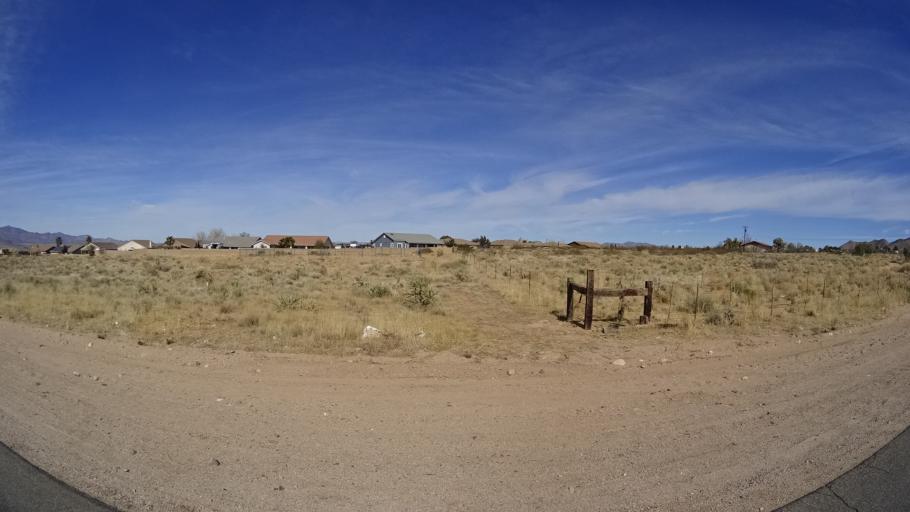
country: US
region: Arizona
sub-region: Mohave County
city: Kingman
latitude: 35.1830
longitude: -114.0005
